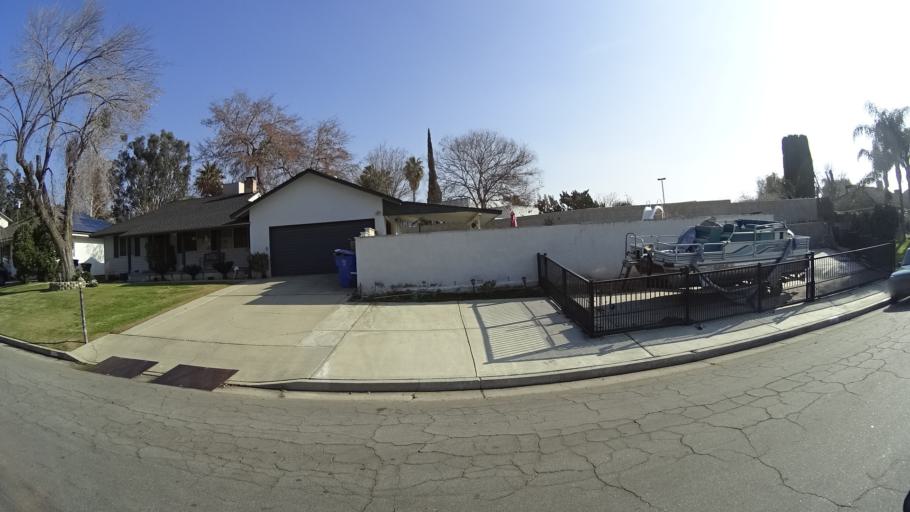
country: US
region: California
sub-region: Kern County
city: Oildale
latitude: 35.4020
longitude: -118.9995
